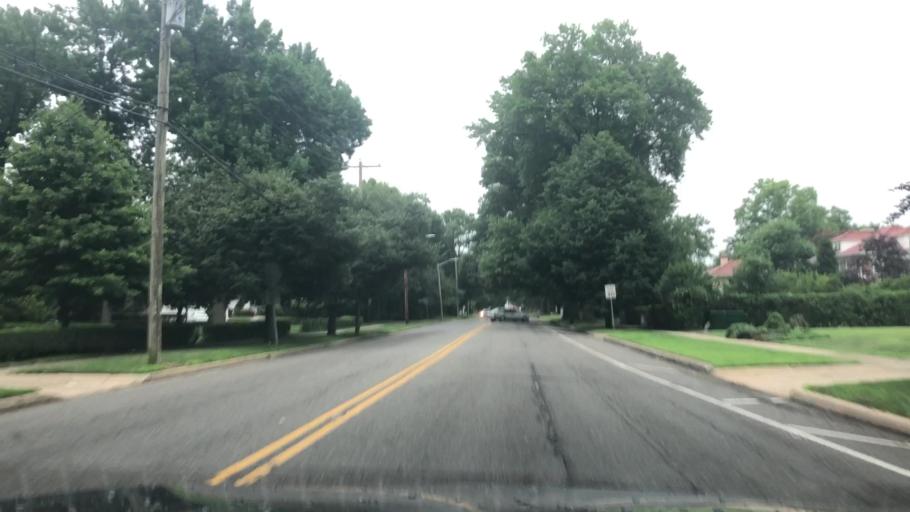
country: US
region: New York
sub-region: Nassau County
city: Garden City
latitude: 40.7127
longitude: -73.6368
